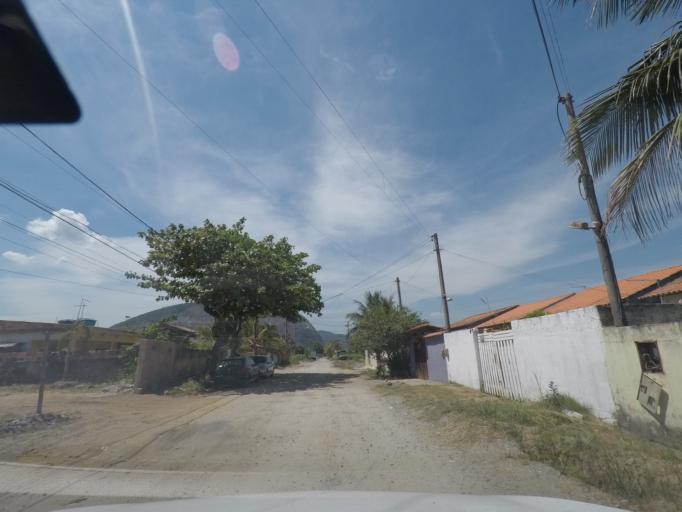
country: BR
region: Rio de Janeiro
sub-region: Marica
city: Marica
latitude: -22.9575
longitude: -42.9577
